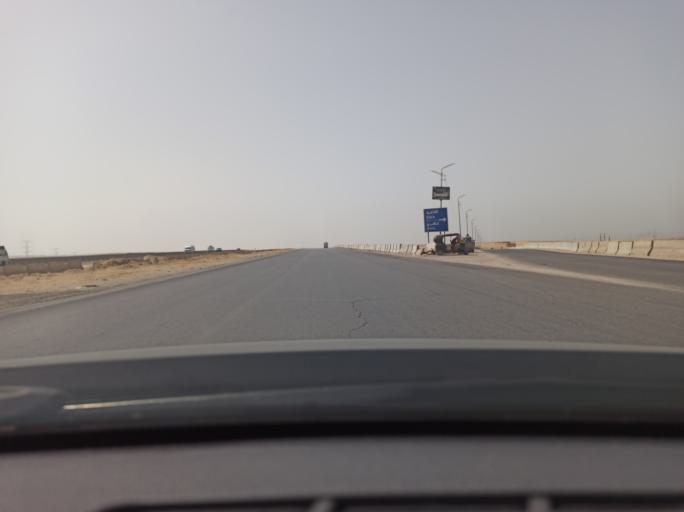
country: EG
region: Muhafazat al Fayyum
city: Al Wasitah
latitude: 29.3791
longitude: 31.3123
